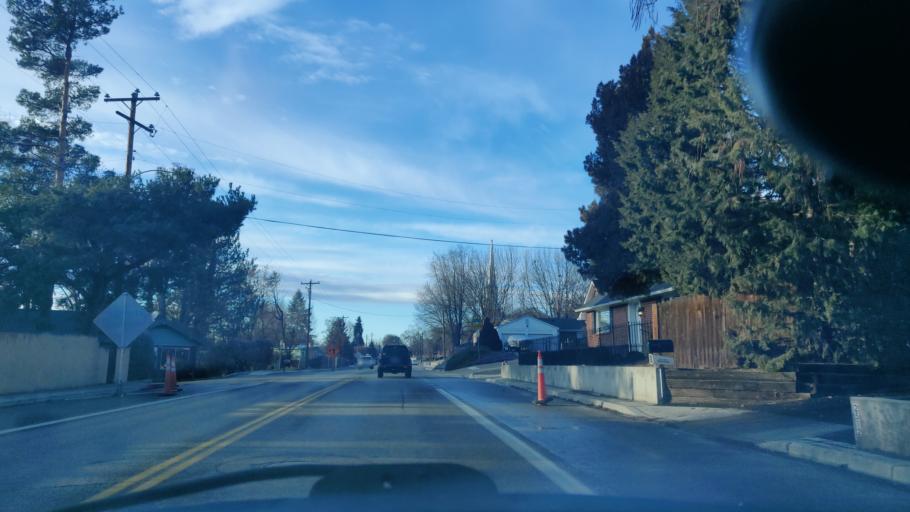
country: US
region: Idaho
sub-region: Ada County
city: Garden City
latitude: 43.6475
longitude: -116.2204
